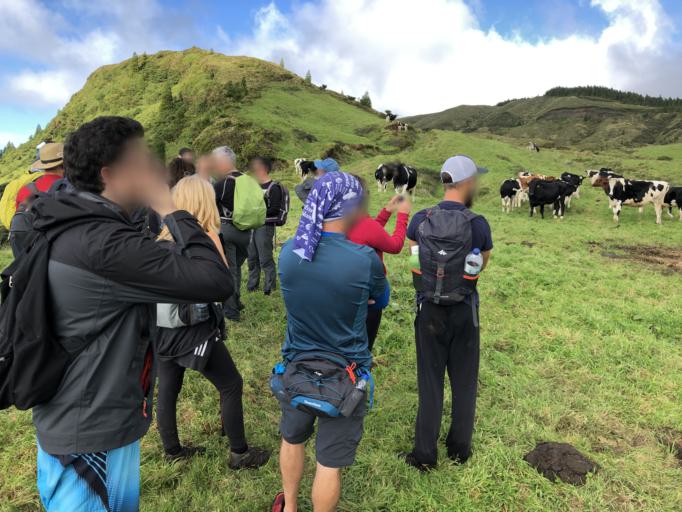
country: PT
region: Azores
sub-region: Ponta Delgada
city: Arrifes
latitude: 37.8316
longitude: -25.7661
